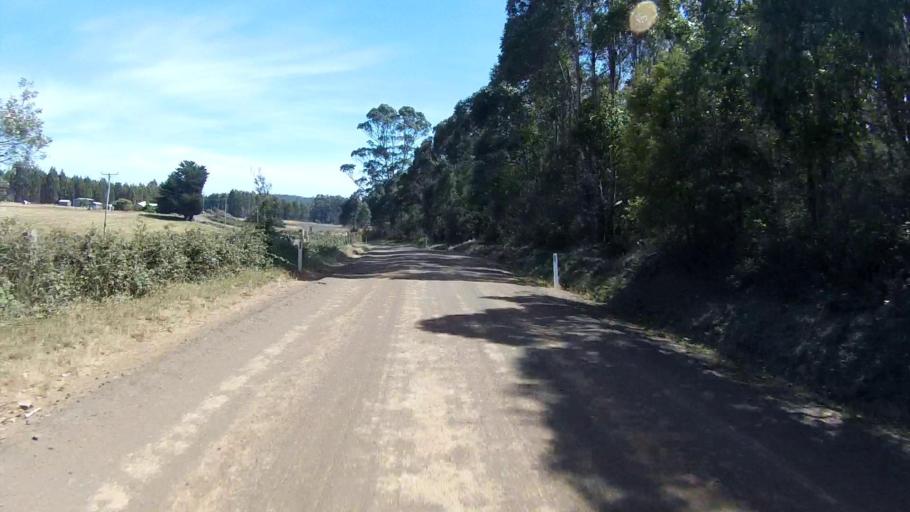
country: AU
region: Tasmania
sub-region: Sorell
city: Sorell
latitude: -42.6977
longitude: 147.7407
